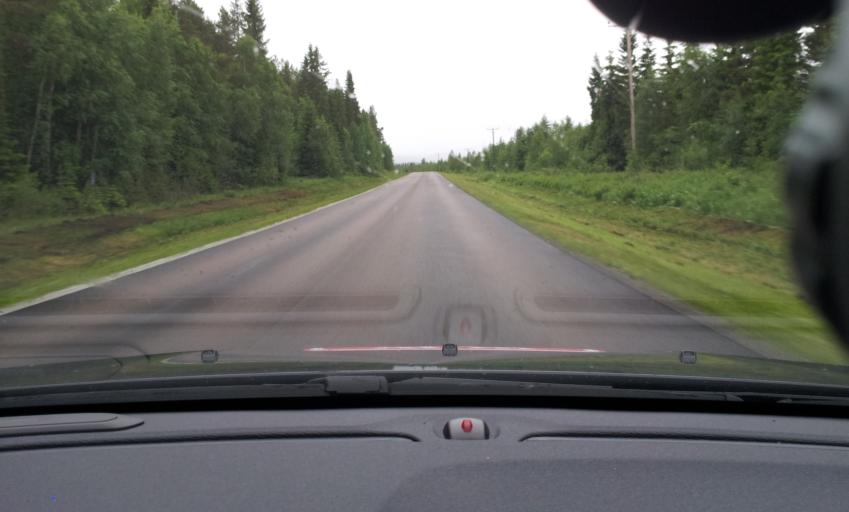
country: SE
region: Jaemtland
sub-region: Ragunda Kommun
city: Hammarstrand
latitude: 63.1970
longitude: 15.9420
